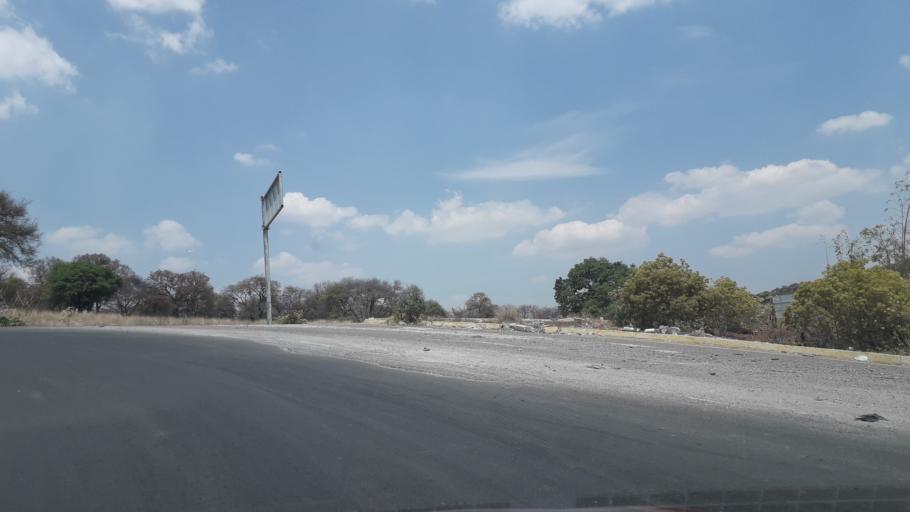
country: MX
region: Puebla
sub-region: Puebla
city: Galaxia la Calera
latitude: 18.9905
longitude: -98.1619
